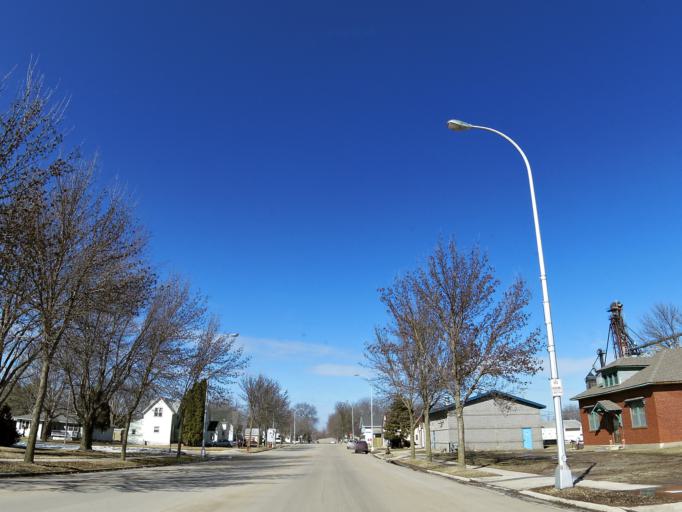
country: US
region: Minnesota
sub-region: Waseca County
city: New Richland
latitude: 43.8955
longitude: -93.4939
